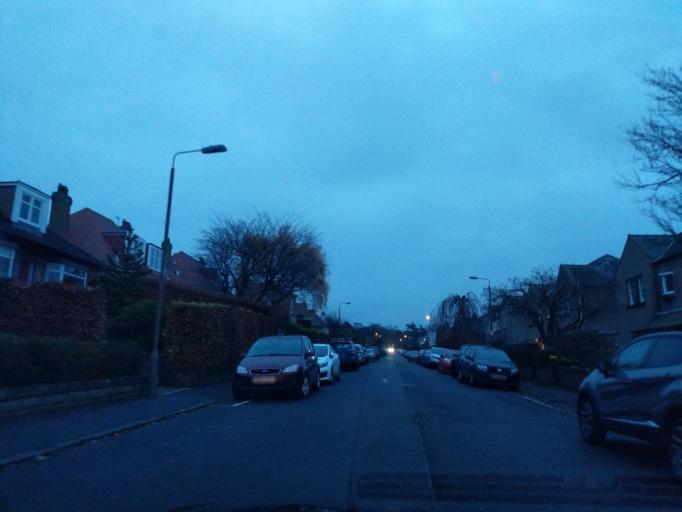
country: GB
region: Scotland
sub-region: Edinburgh
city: Colinton
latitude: 55.9450
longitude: -3.2785
